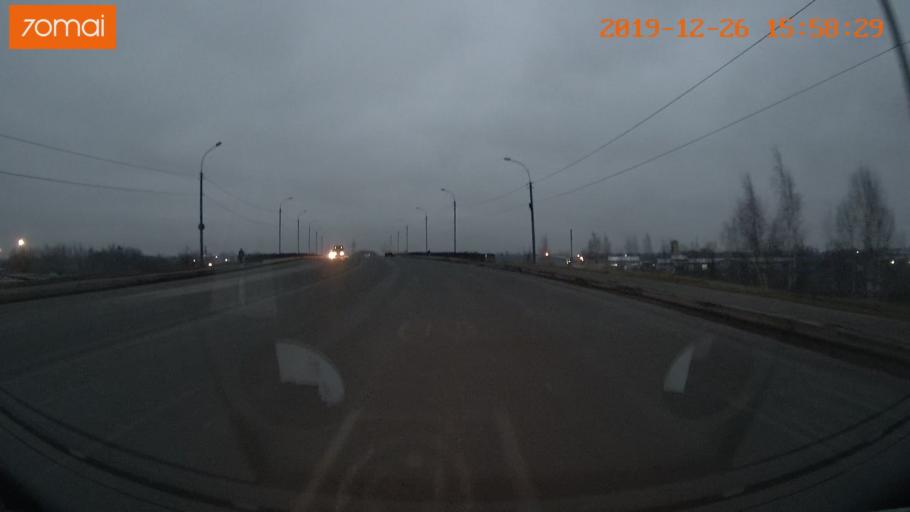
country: RU
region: Jaroslavl
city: Rybinsk
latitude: 58.0387
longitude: 38.7963
